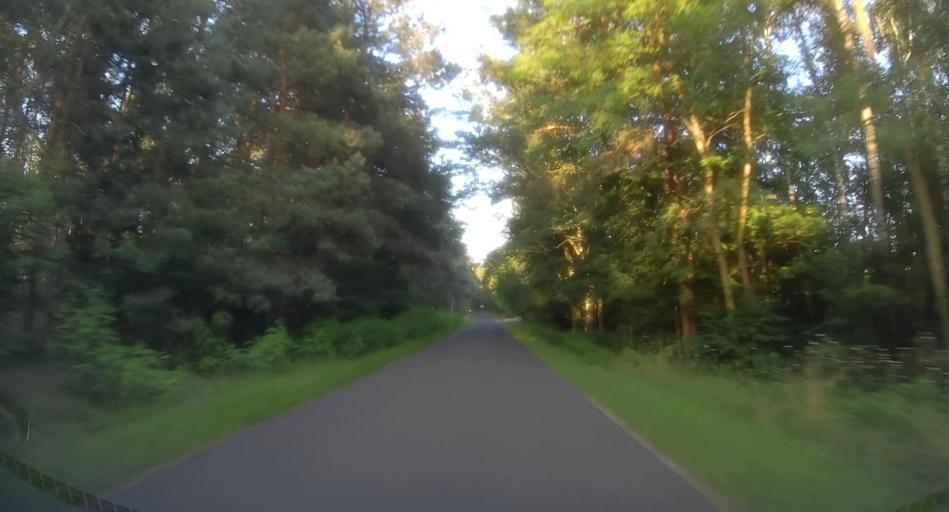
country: PL
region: Masovian Voivodeship
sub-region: Powiat zyrardowski
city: Puszcza Marianska
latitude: 51.9067
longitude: 20.3355
